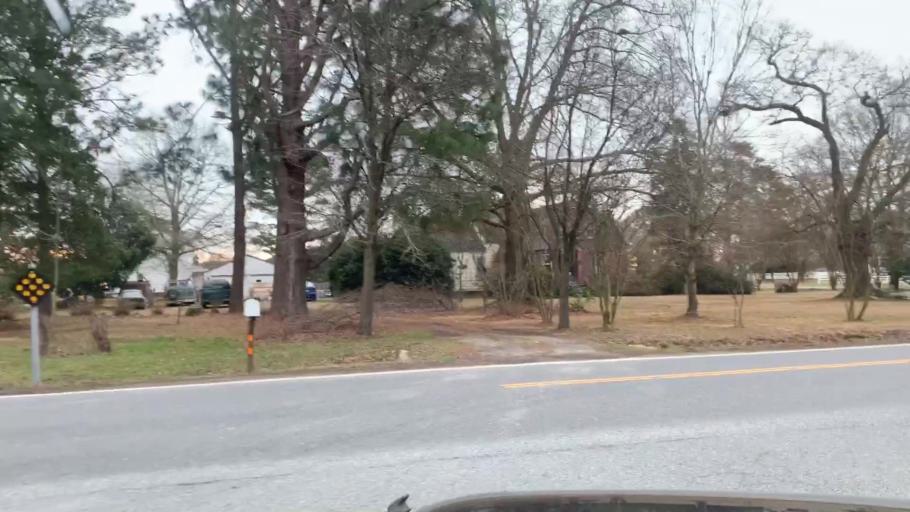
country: US
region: North Carolina
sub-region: Currituck County
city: Moyock
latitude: 36.6410
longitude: -76.2042
